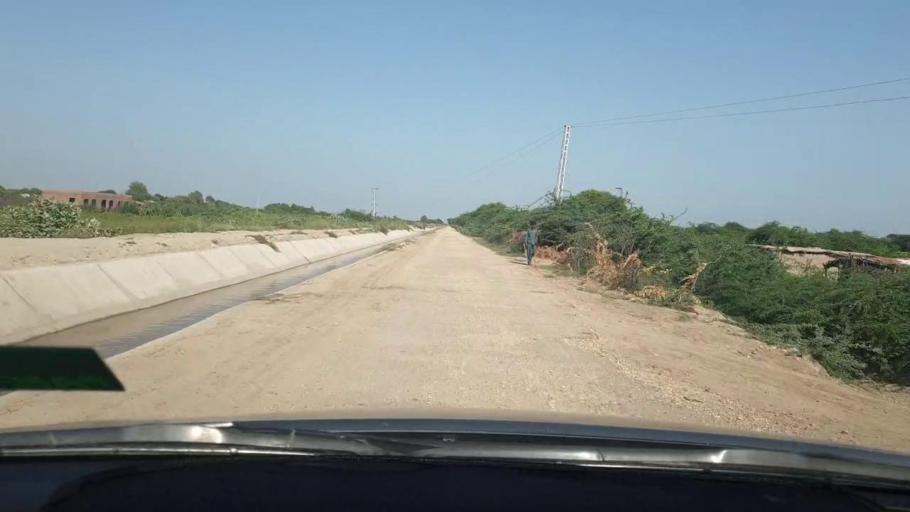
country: PK
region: Sindh
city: Naukot
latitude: 24.9298
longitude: 69.2641
